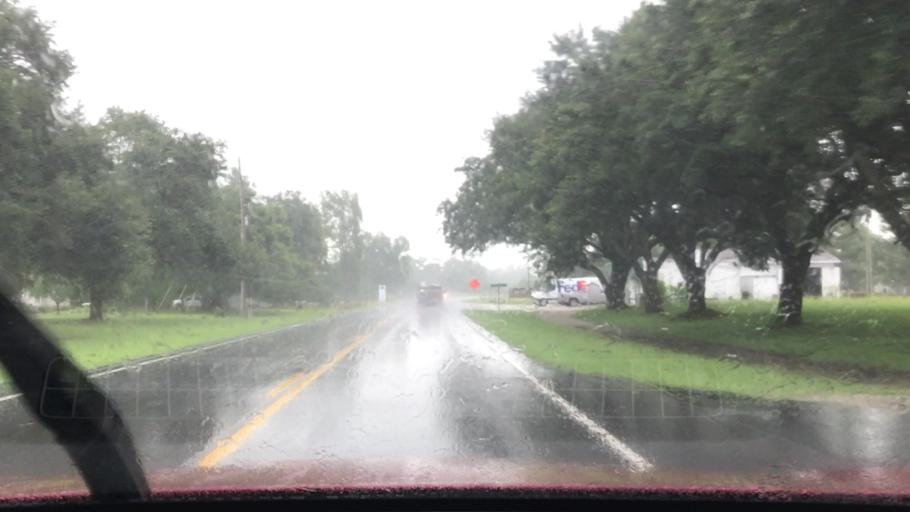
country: US
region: South Carolina
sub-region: Horry County
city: Loris
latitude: 33.9021
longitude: -78.8863
